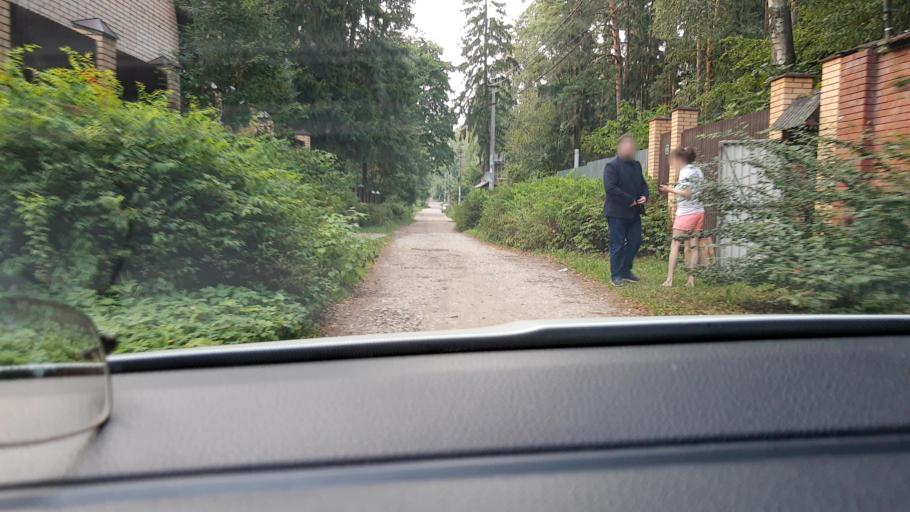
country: RU
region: Moskovskaya
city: Kratovo
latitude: 55.6007
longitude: 38.1622
